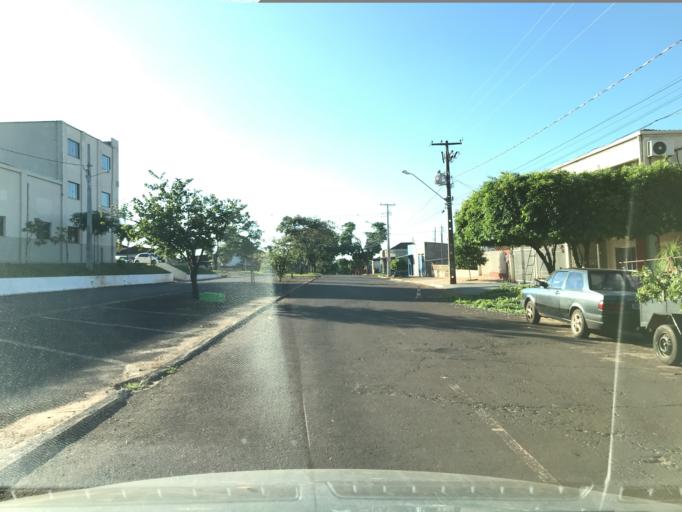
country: BR
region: Parana
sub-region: Ipora
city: Ipora
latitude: -24.0020
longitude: -53.7169
